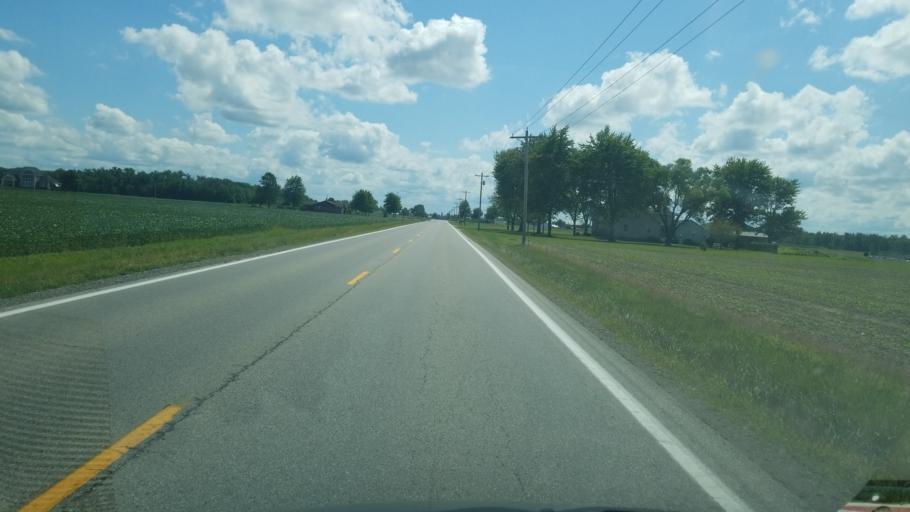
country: US
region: Ohio
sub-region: Putnam County
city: Kalida
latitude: 41.0239
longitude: -84.1981
